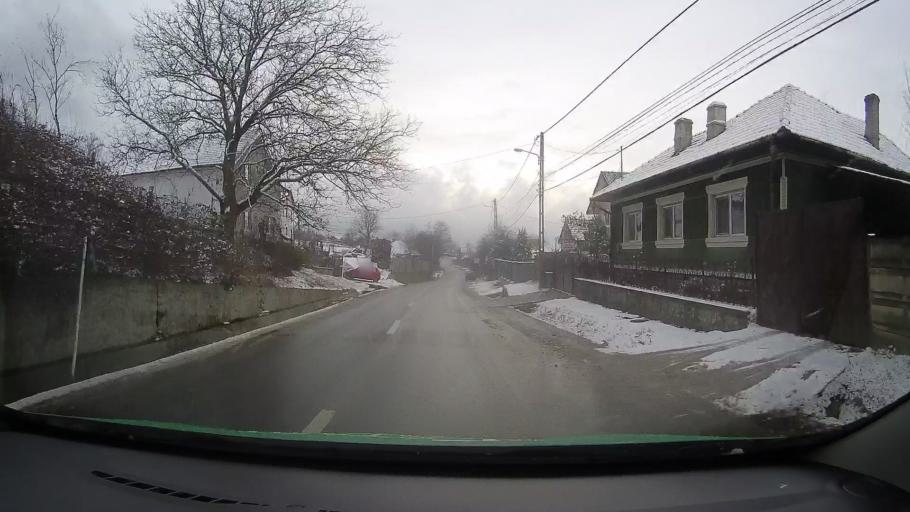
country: RO
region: Hunedoara
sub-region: Oras Hateg
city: Hateg
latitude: 45.6244
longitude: 22.9368
